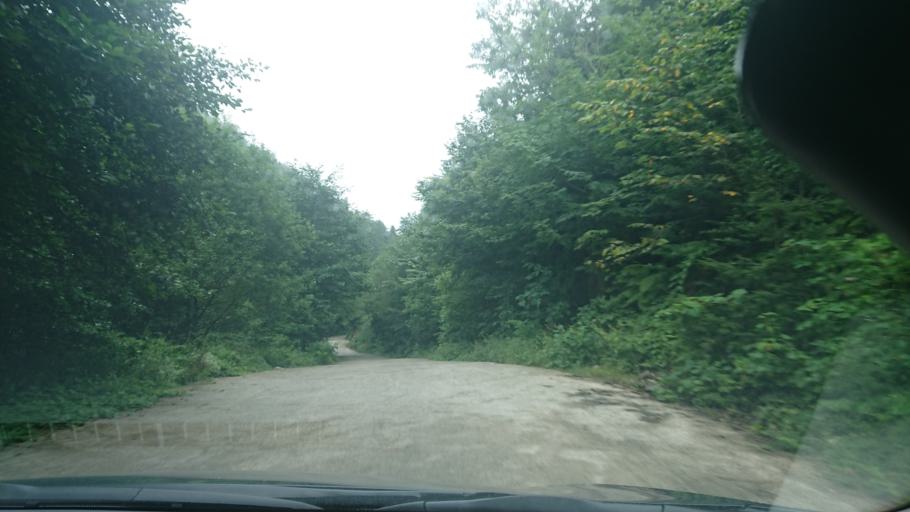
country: TR
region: Gumushane
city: Kurtun
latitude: 40.6638
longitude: 39.0353
